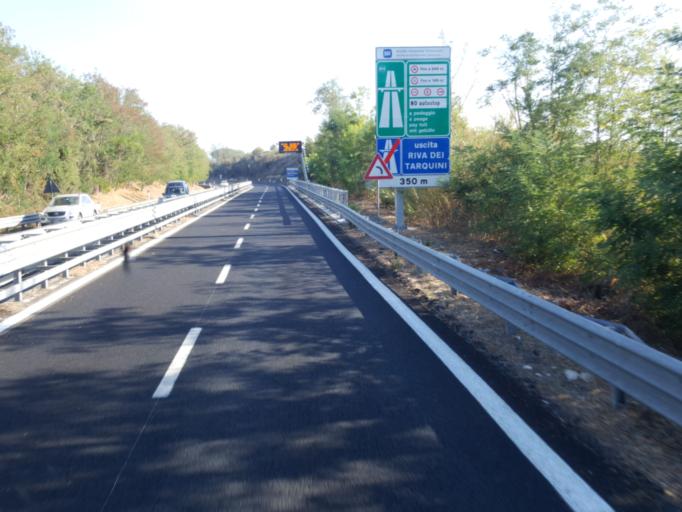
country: IT
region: Latium
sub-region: Provincia di Viterbo
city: Montalto di Castro
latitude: 42.3133
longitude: 11.6539
